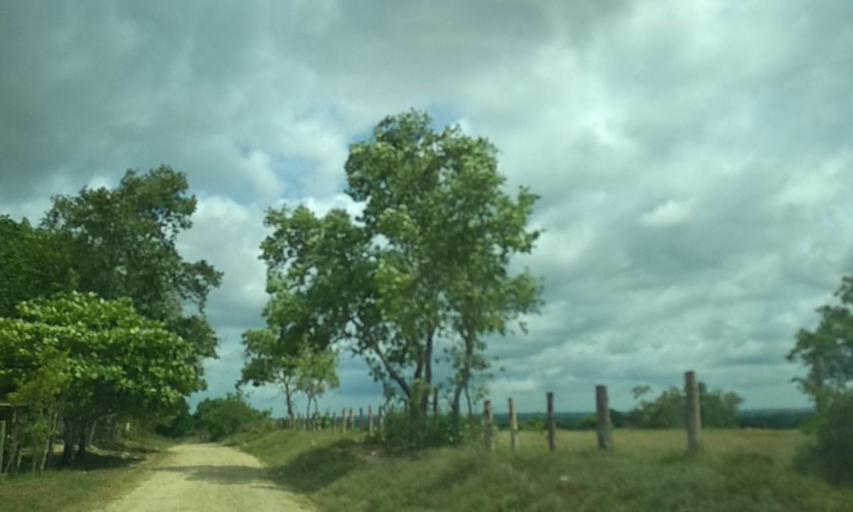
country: MX
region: Veracruz
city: Las Choapas
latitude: 17.8935
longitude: -94.1168
